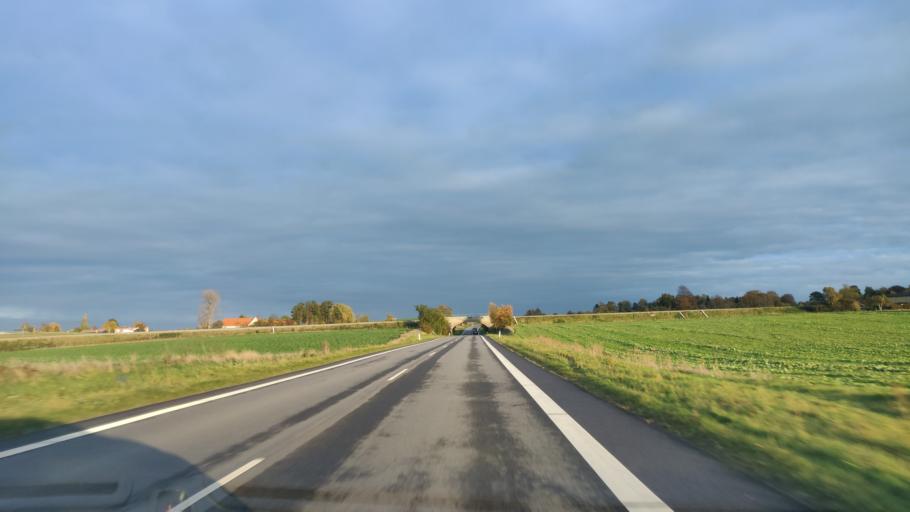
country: DK
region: Zealand
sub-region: Holbaek Kommune
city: Vipperod
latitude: 55.6836
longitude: 11.7207
